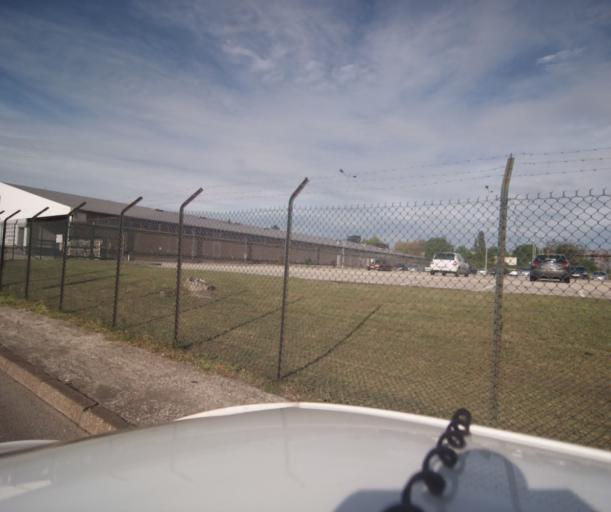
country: FR
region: Franche-Comte
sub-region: Departement du Doubs
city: Besancon
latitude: 47.2401
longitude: 5.9938
